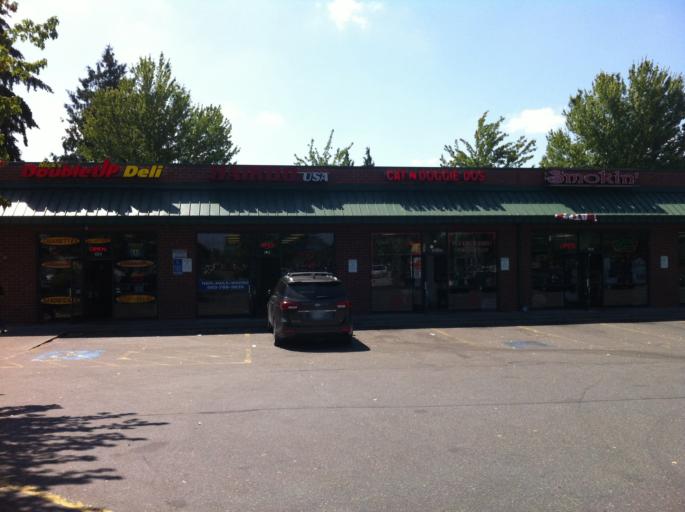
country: US
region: Oregon
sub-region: Multnomah County
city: Lents
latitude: 45.4972
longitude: -122.5799
